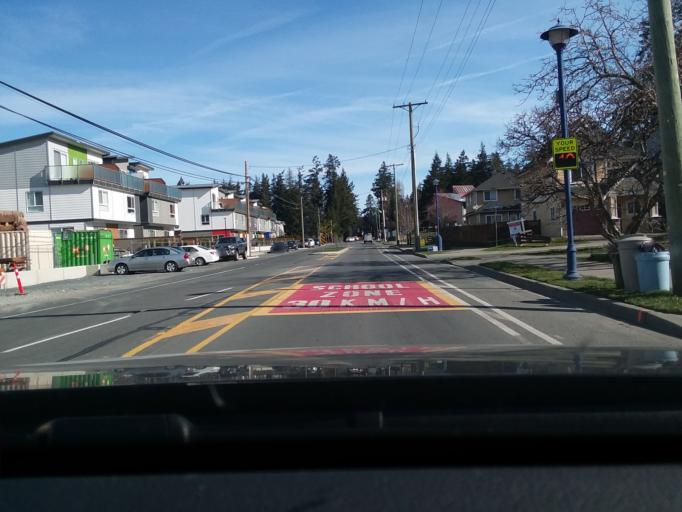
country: CA
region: British Columbia
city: Langford
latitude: 48.4270
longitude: -123.5305
